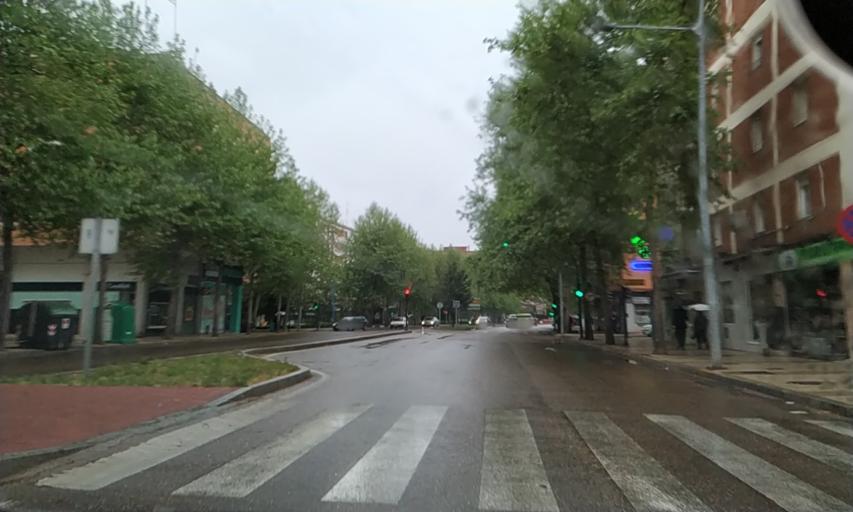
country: ES
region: Extremadura
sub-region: Provincia de Badajoz
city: Badajoz
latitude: 38.8670
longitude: -6.9730
